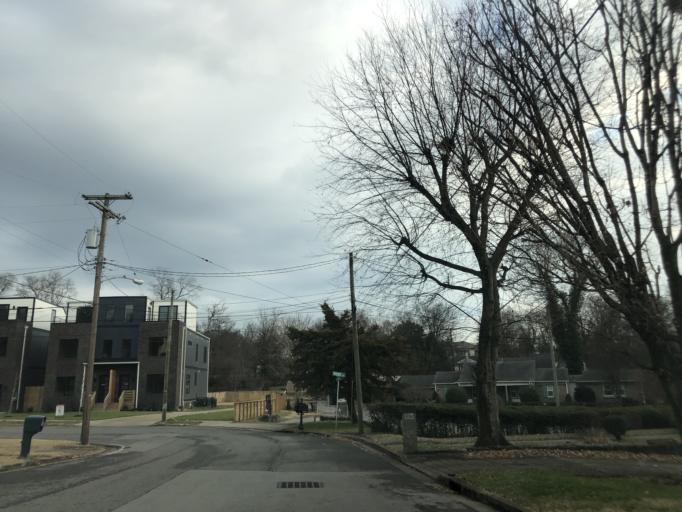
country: US
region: Tennessee
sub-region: Davidson County
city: Nashville
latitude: 36.1987
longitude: -86.7382
